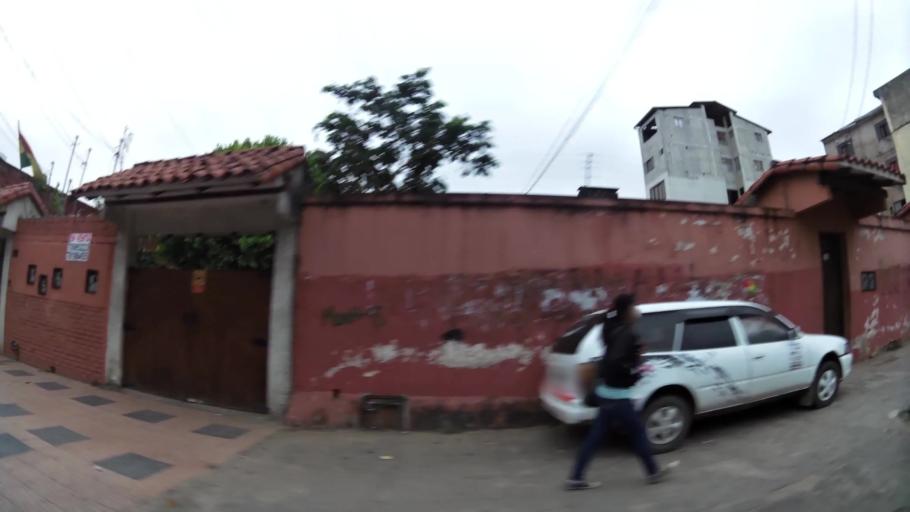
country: BO
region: Santa Cruz
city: Santa Cruz de la Sierra
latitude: -17.7803
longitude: -63.1865
